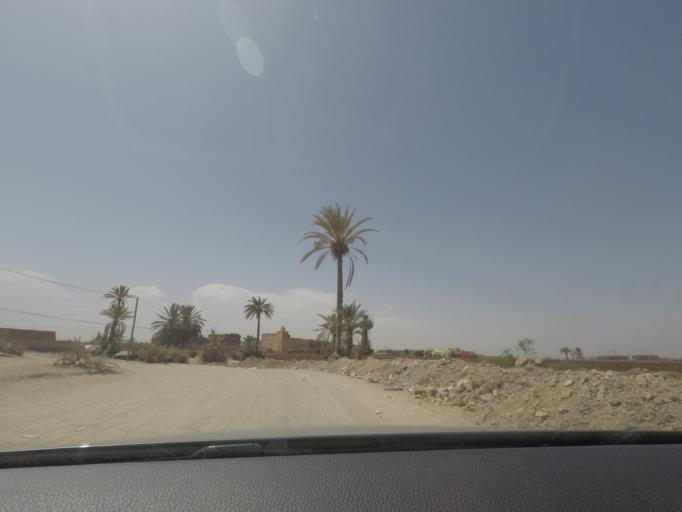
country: MA
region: Marrakech-Tensift-Al Haouz
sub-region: Marrakech
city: Marrakesh
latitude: 31.5826
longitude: -8.0300
